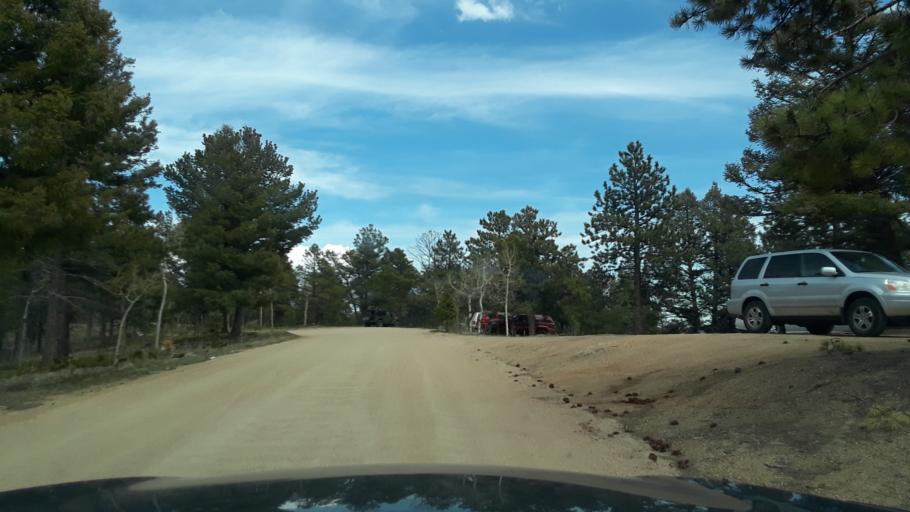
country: US
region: Colorado
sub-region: El Paso County
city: Palmer Lake
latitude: 39.0585
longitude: -104.9806
